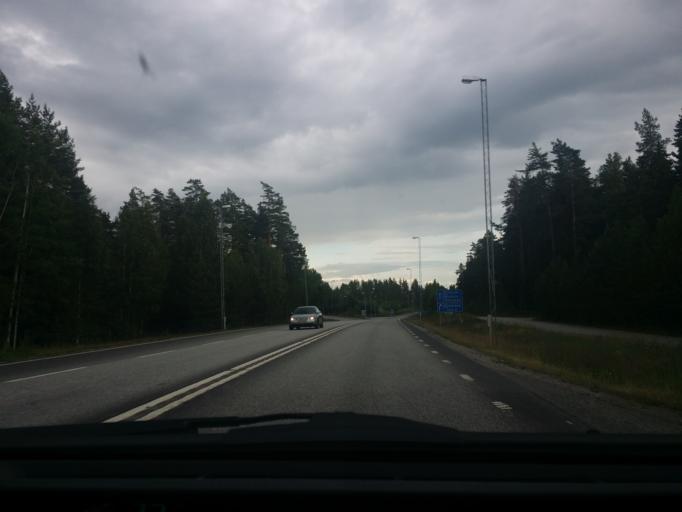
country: SE
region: OErebro
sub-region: Nora Kommun
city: Nora
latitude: 59.4722
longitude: 15.1280
